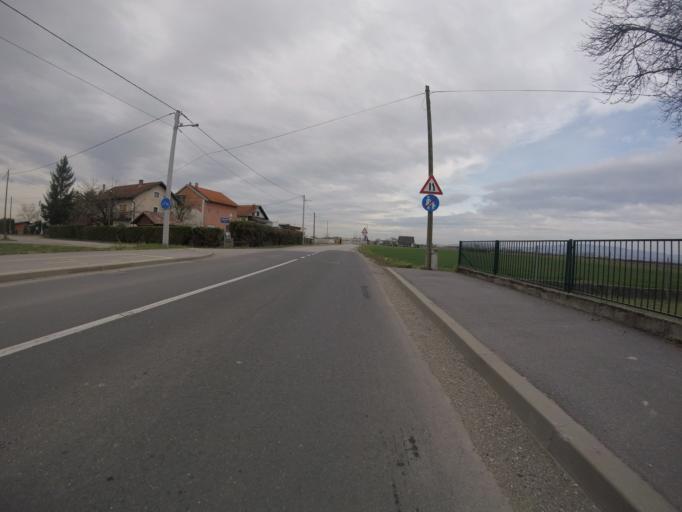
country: HR
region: Zagrebacka
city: Gradici
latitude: 45.7100
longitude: 16.0338
